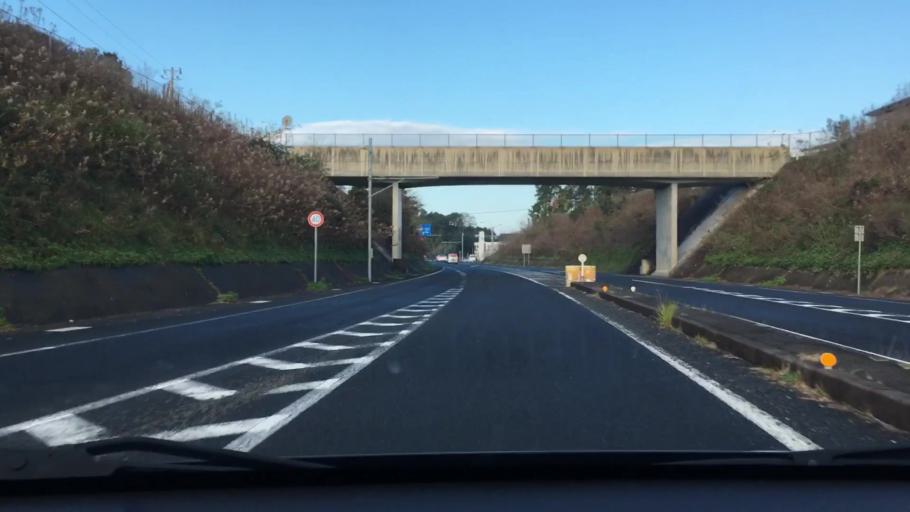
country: JP
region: Nagasaki
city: Sasebo
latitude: 33.0446
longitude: 129.7468
